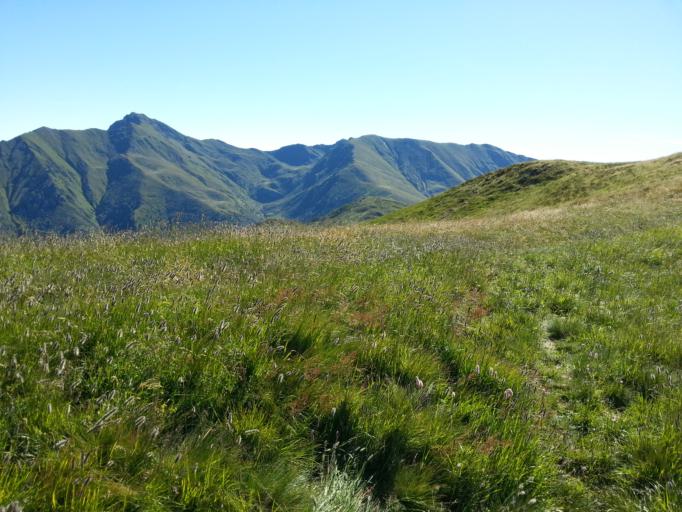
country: CH
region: Ticino
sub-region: Bellinzona District
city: Camorino
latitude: 46.1080
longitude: 9.0110
